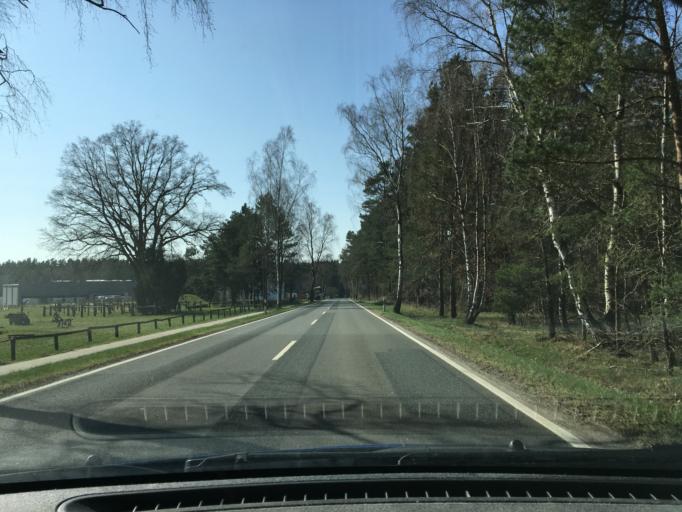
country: DE
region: Lower Saxony
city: Hermannsburg
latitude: 52.8255
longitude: 10.1175
